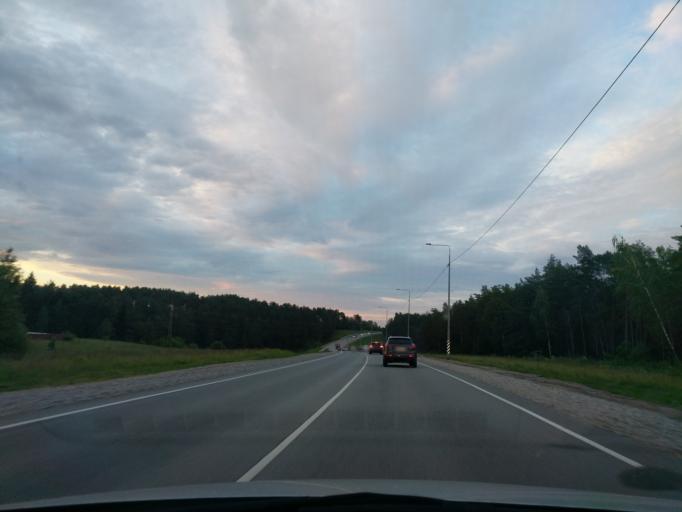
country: RU
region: Kaluga
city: Maloyaroslavets
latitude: 55.0424
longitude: 36.5482
